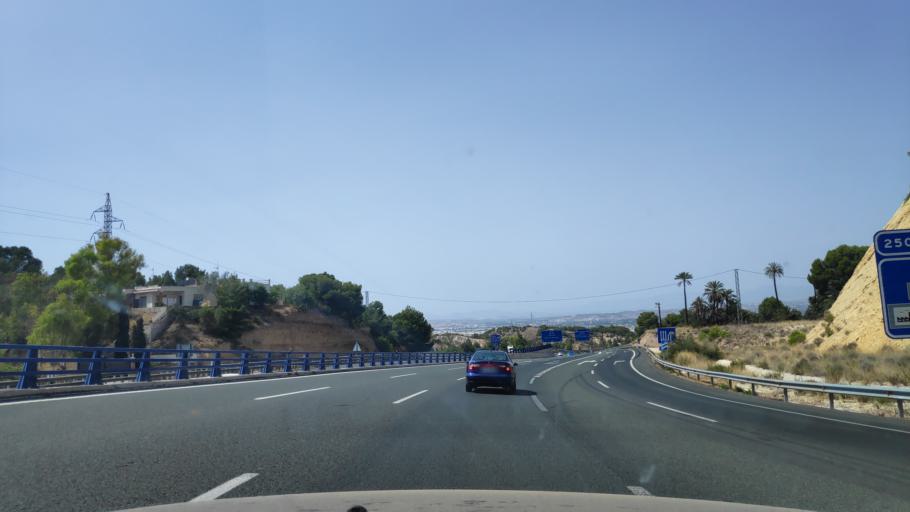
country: ES
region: Murcia
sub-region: Murcia
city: Alcantarilla
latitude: 37.9100
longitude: -1.1630
